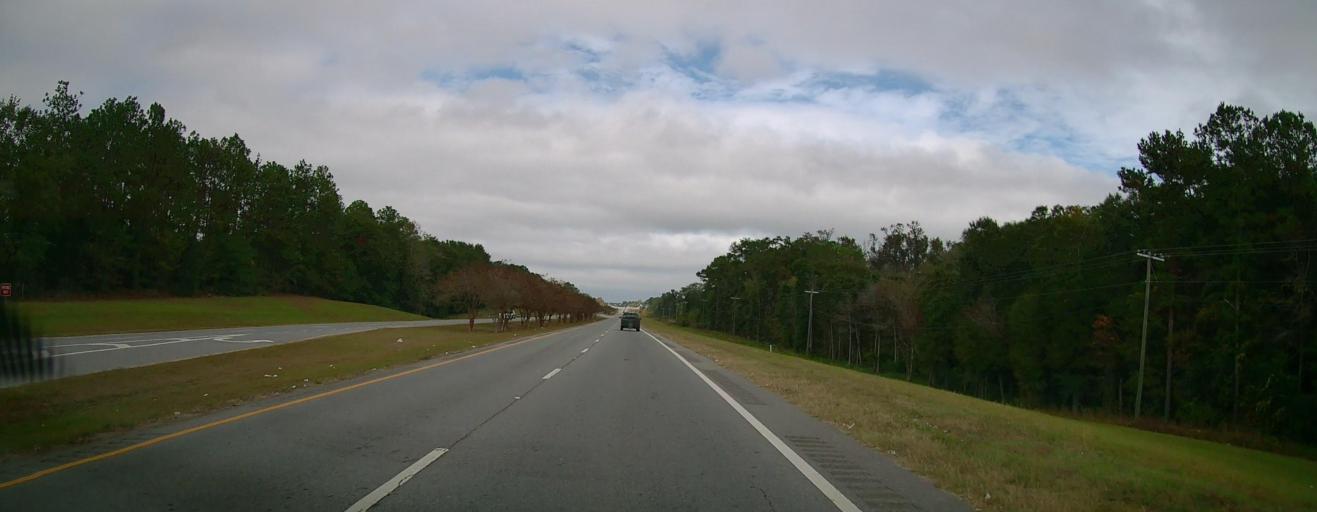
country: US
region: Georgia
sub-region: Colquitt County
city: Moultrie
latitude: 31.1562
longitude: -83.7616
